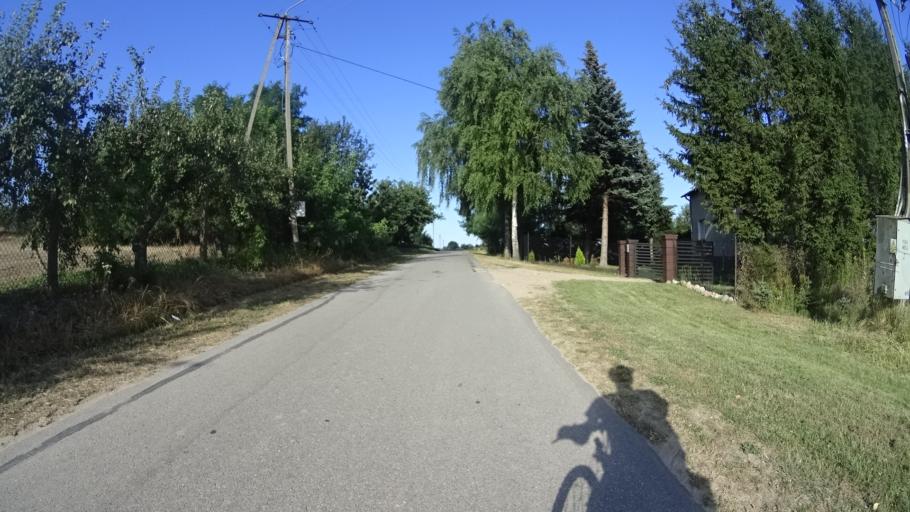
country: PL
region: Masovian Voivodeship
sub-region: Powiat grojecki
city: Goszczyn
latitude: 51.6827
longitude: 20.8301
